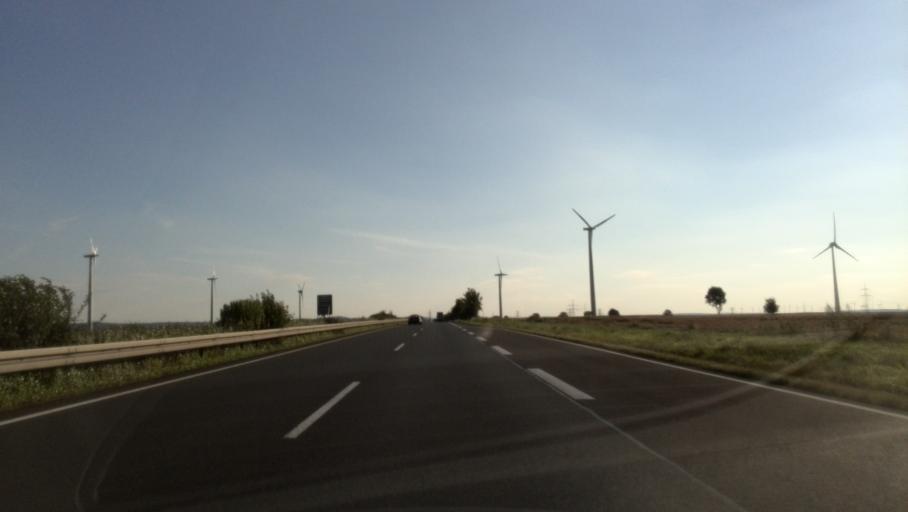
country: DE
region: Lower Saxony
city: Vechelde
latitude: 52.1882
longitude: 10.3935
